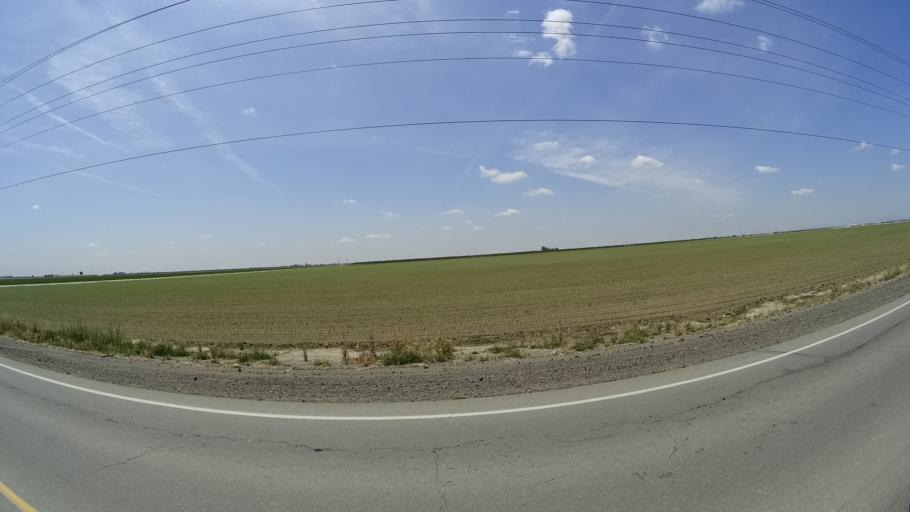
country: US
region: California
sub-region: Tulare County
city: Goshen
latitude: 36.2980
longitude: -119.5032
